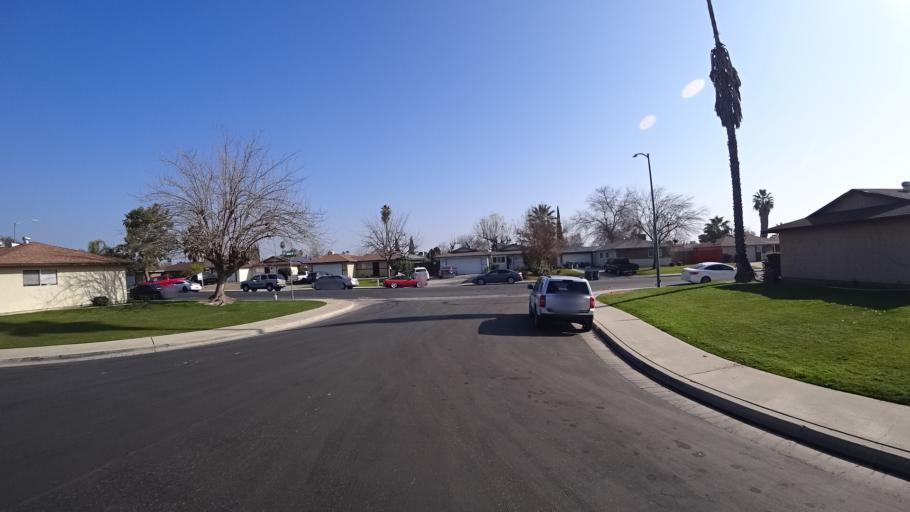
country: US
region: California
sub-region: Kern County
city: Bakersfield
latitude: 35.3224
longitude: -119.0629
